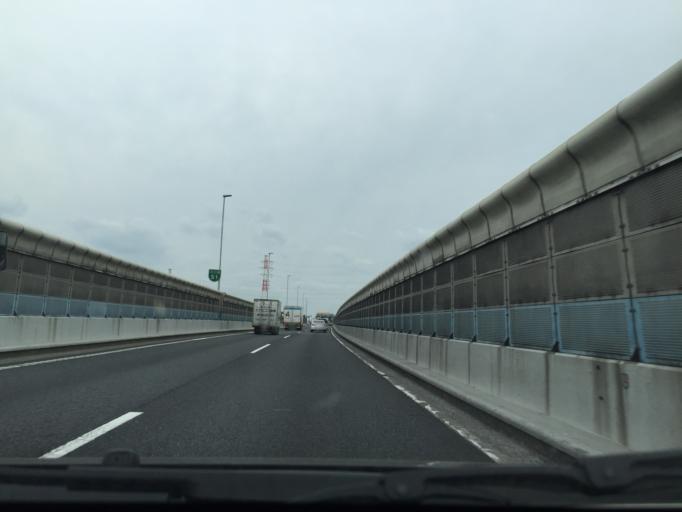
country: JP
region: Saitama
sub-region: Kawaguchi-shi
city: Hatogaya-honcho
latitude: 35.8351
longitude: 139.7559
